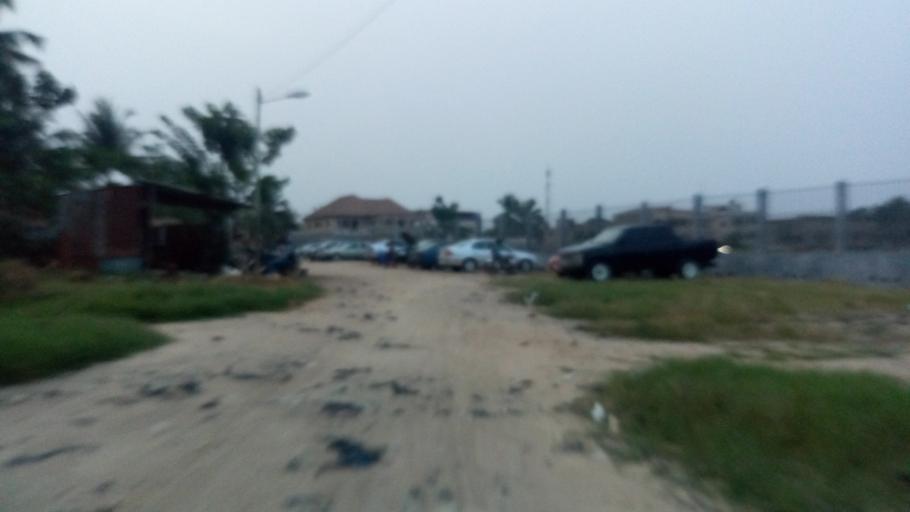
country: TG
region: Maritime
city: Lome
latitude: 6.1767
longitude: 1.1766
